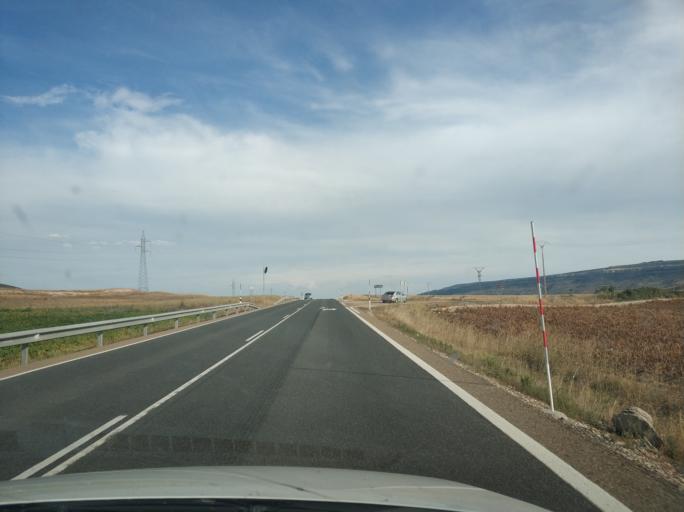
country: ES
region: Castille and Leon
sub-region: Provincia de Palencia
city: Pomar de Valdivia
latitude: 42.7501
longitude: -4.1687
